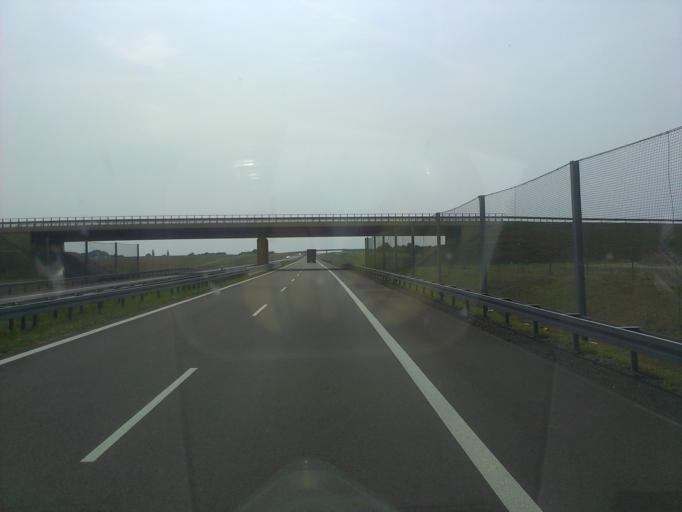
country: PL
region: Lubusz
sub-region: Powiat zielonogorski
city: Sulechow
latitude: 52.1202
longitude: 15.5778
